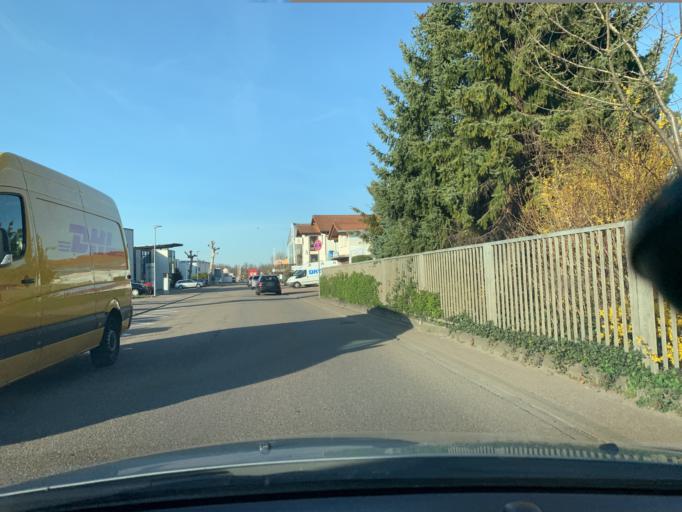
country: DE
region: Baden-Wuerttemberg
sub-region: Freiburg Region
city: Umkirch
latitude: 48.0412
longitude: 7.7659
